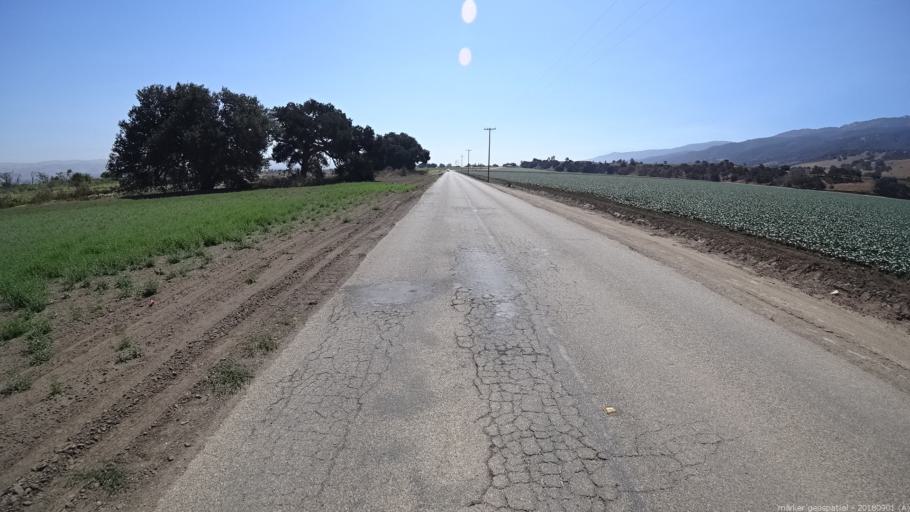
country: US
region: California
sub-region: Monterey County
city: Chualar
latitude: 36.5300
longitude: -121.5308
